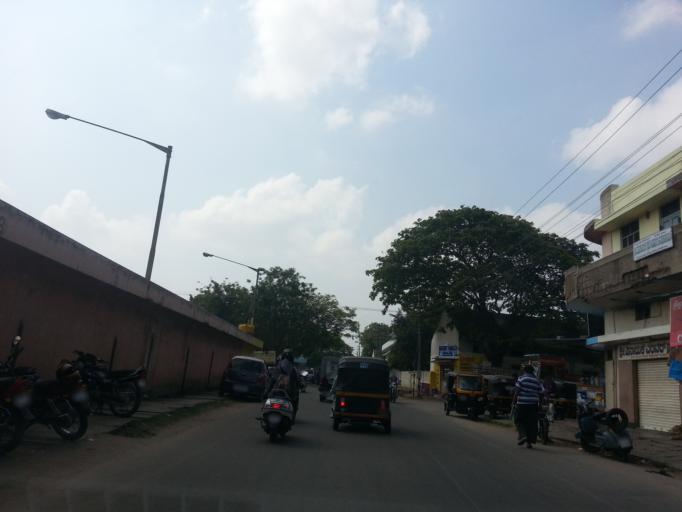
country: IN
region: Karnataka
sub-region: Mysore
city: Mysore
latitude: 12.3189
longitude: 76.6478
